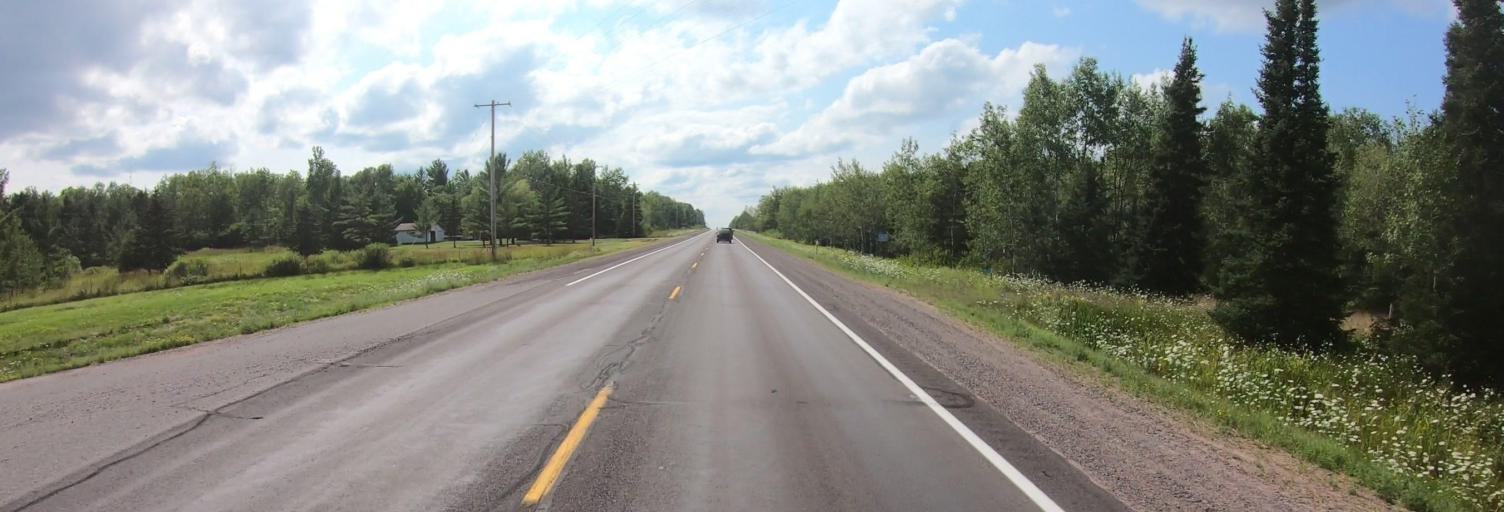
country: US
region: Michigan
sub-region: Ontonagon County
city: Ontonagon
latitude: 46.5348
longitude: -89.2407
